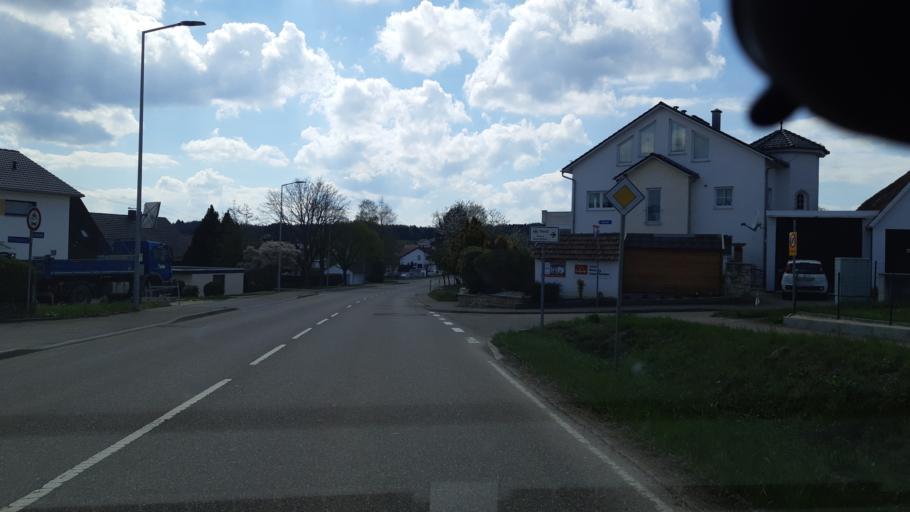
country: DE
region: Baden-Wuerttemberg
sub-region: Regierungsbezirk Stuttgart
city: Westhausen
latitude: 48.8043
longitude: 10.1880
